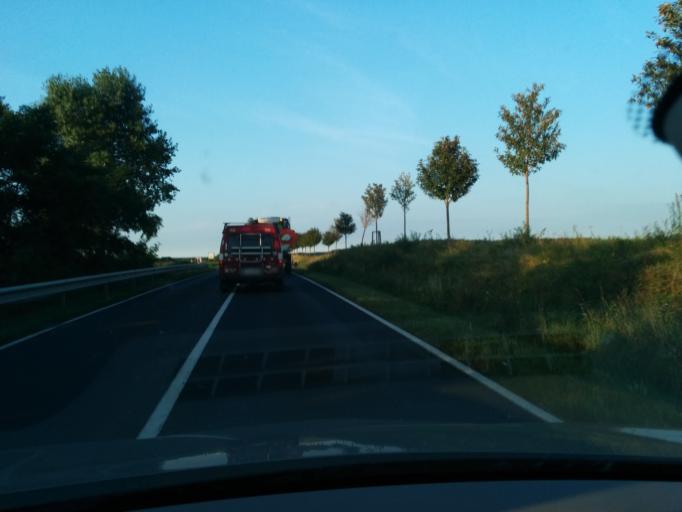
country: DE
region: Mecklenburg-Vorpommern
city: Loddin
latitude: 53.9488
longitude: 14.0496
